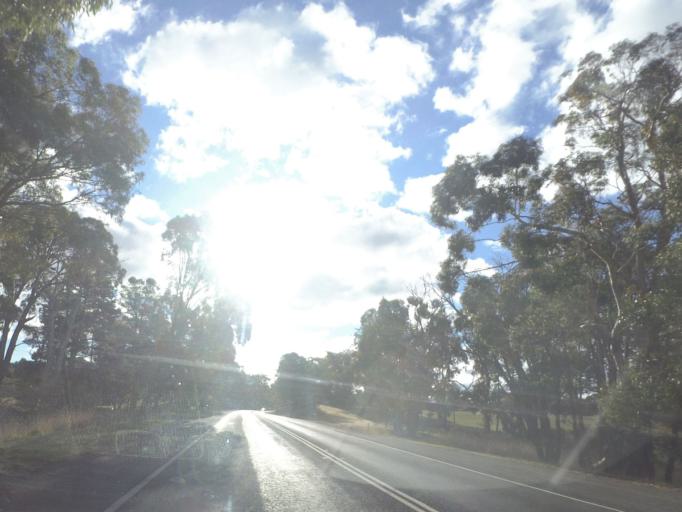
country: AU
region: Victoria
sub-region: Mount Alexander
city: Castlemaine
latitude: -37.1228
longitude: 144.3426
